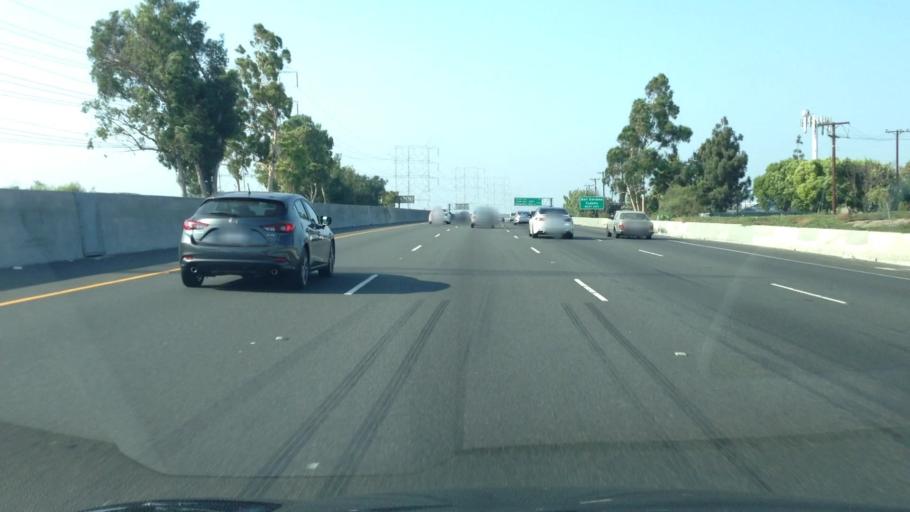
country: US
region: California
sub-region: Los Angeles County
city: Cudahy
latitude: 33.9544
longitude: -118.1705
